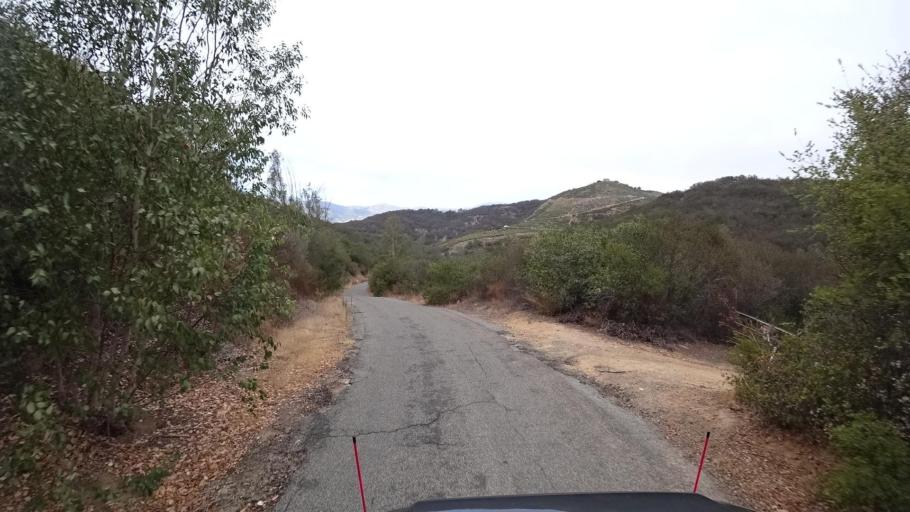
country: US
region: California
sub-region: San Diego County
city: Fallbrook
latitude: 33.4412
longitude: -117.3039
